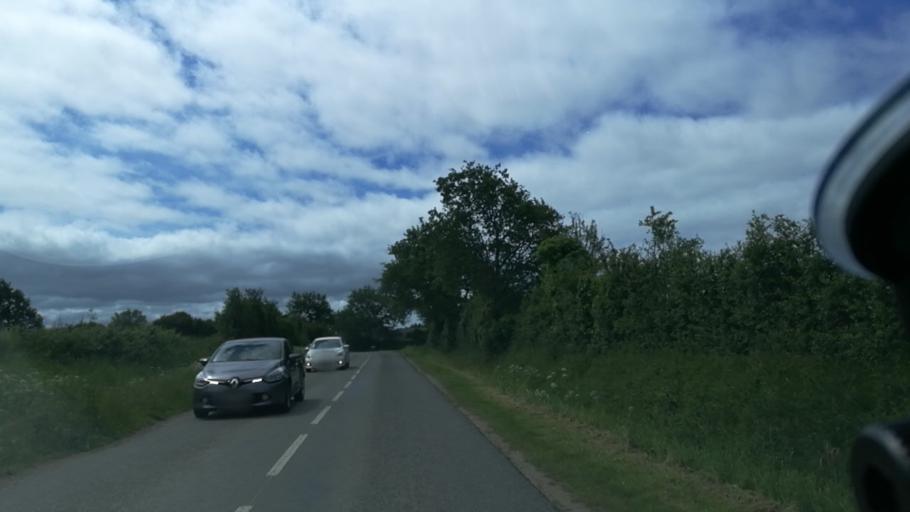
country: FR
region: Brittany
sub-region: Departement du Morbihan
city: Penestin
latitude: 47.4685
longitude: -2.4316
